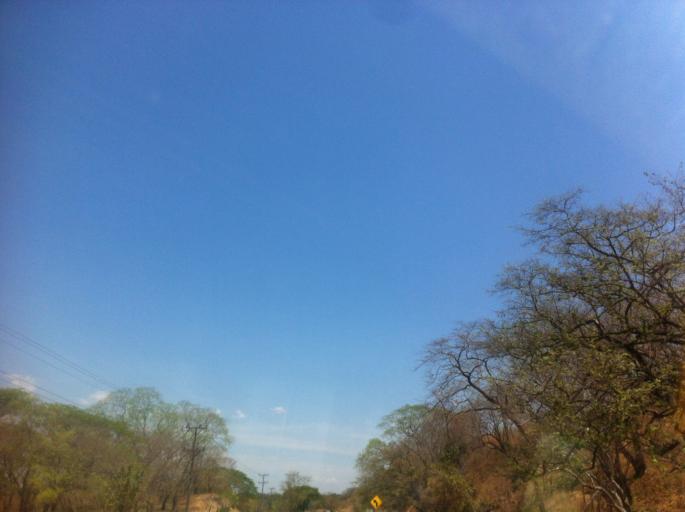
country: CR
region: Guanacaste
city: Sardinal
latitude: 10.5277
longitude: -85.5852
